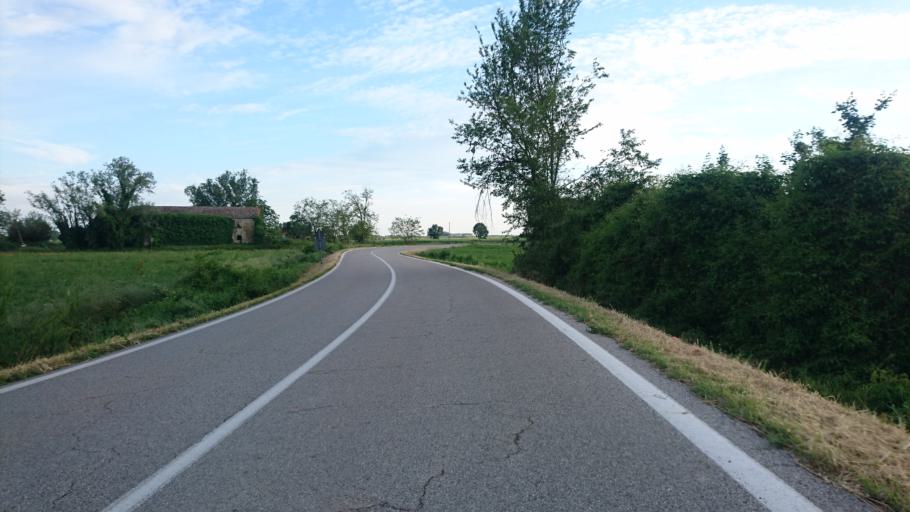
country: IT
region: Veneto
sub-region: Provincia di Rovigo
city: Ceneselli
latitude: 45.0211
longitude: 11.3463
